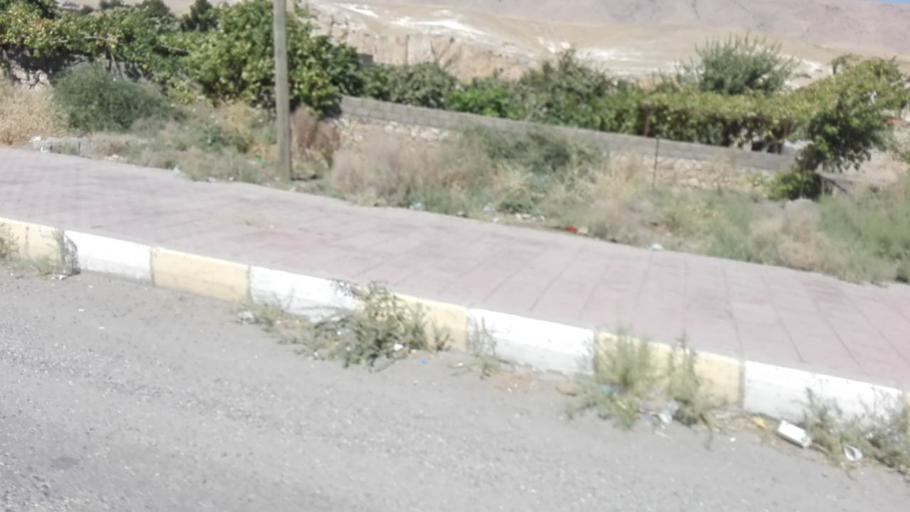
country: TR
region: Batman
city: Hasankeyf
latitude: 37.7133
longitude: 41.4219
